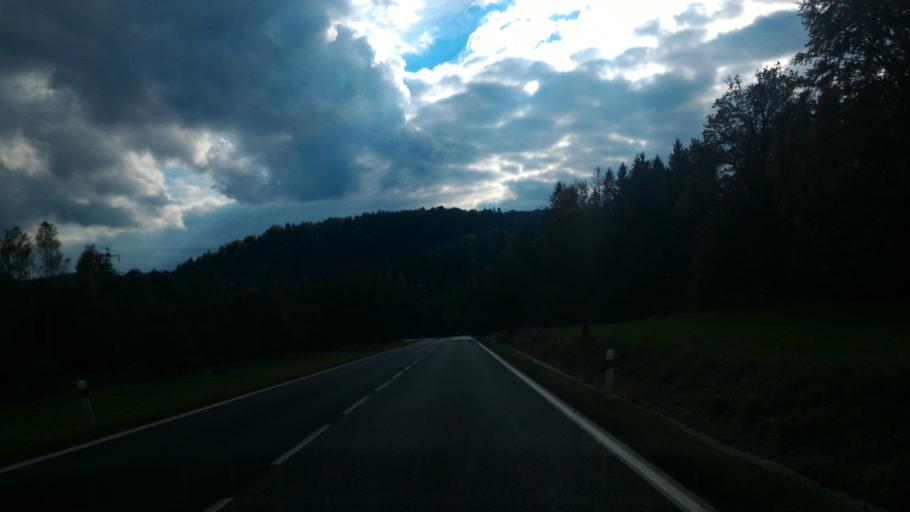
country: CZ
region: Ustecky
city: Ceska Kamenice
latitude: 50.8150
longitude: 14.4401
